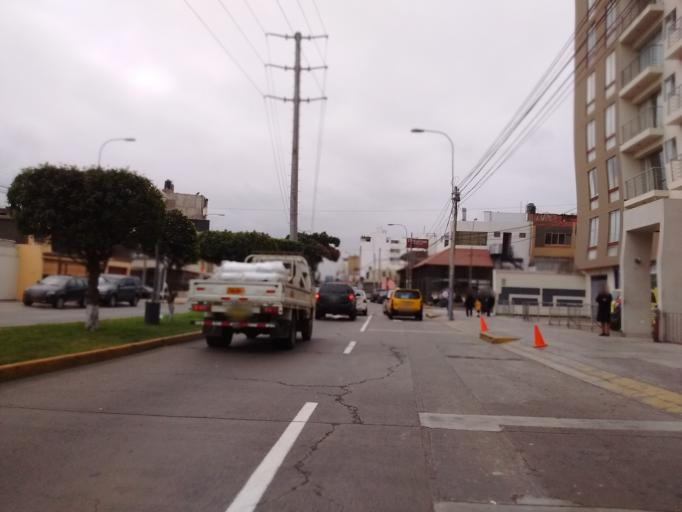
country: PE
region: Callao
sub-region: Callao
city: Callao
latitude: -12.0745
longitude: -77.0921
